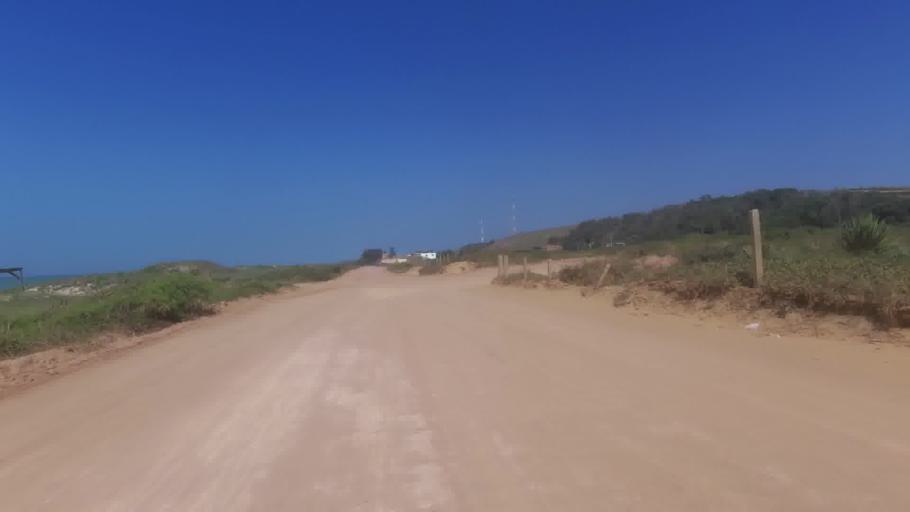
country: BR
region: Espirito Santo
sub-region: Marataizes
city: Marataizes
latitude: -21.0973
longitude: -40.8470
